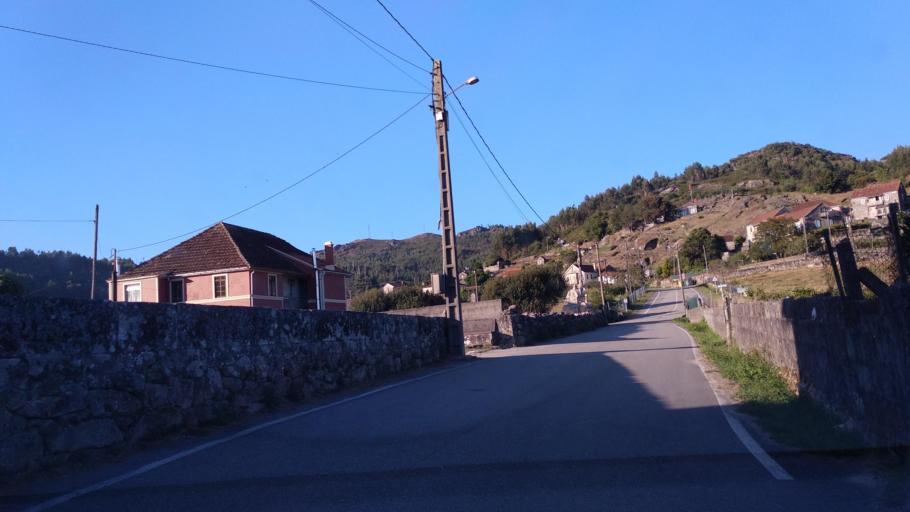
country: ES
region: Galicia
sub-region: Provincia de Pontevedra
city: Ponte Caldelas
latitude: 42.3575
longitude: -8.4908
